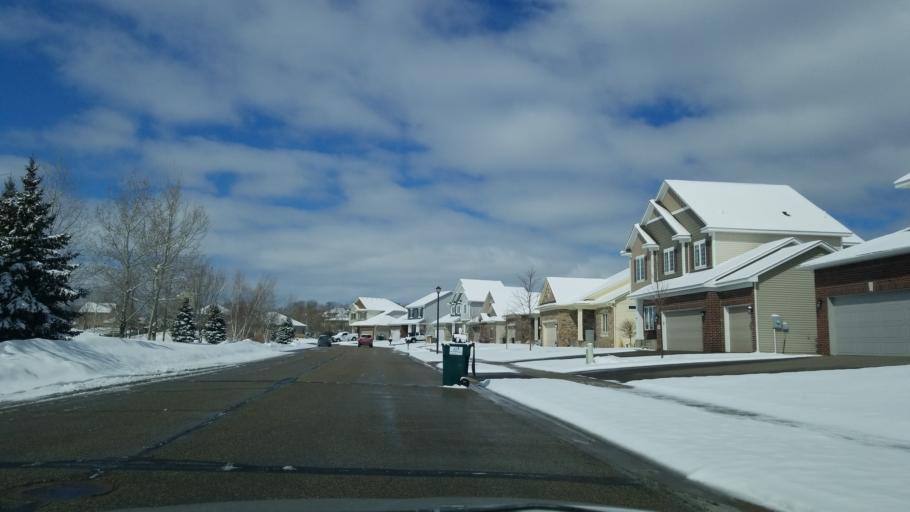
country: US
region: Wisconsin
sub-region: Saint Croix County
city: Hudson
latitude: 44.9542
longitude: -92.7074
